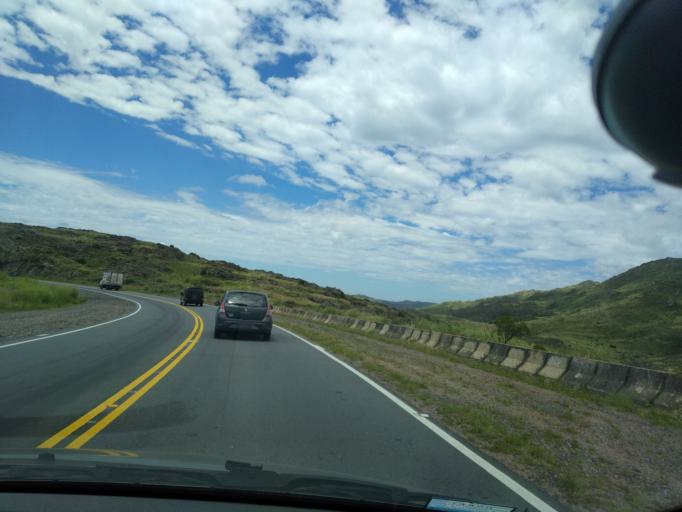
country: AR
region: Cordoba
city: Cuesta Blanca
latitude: -31.6372
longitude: -64.6804
